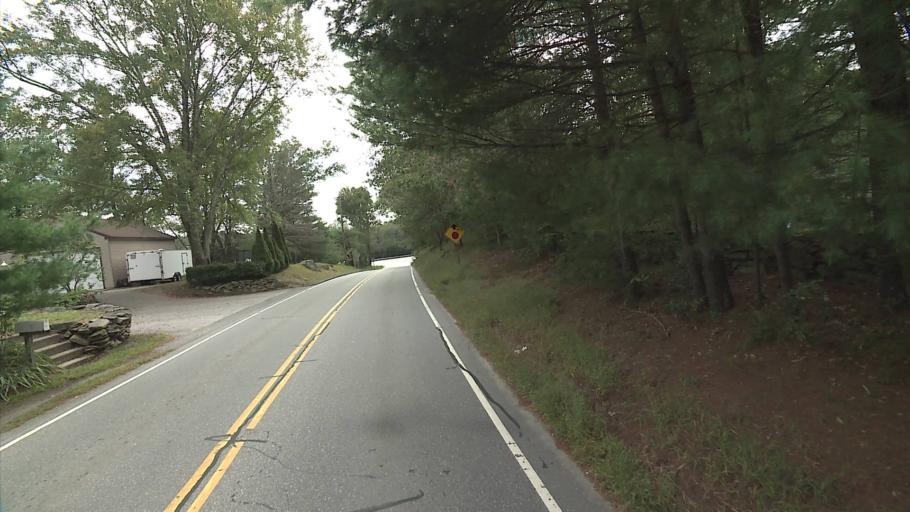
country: US
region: Connecticut
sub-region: New London County
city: Jewett City
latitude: 41.6375
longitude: -71.9551
